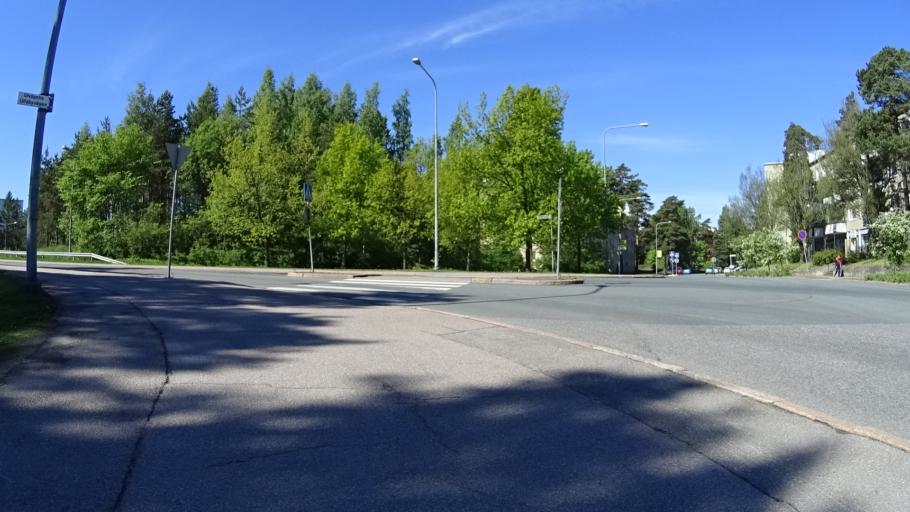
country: FI
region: Uusimaa
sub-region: Helsinki
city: Teekkarikylae
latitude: 60.2038
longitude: 24.8725
